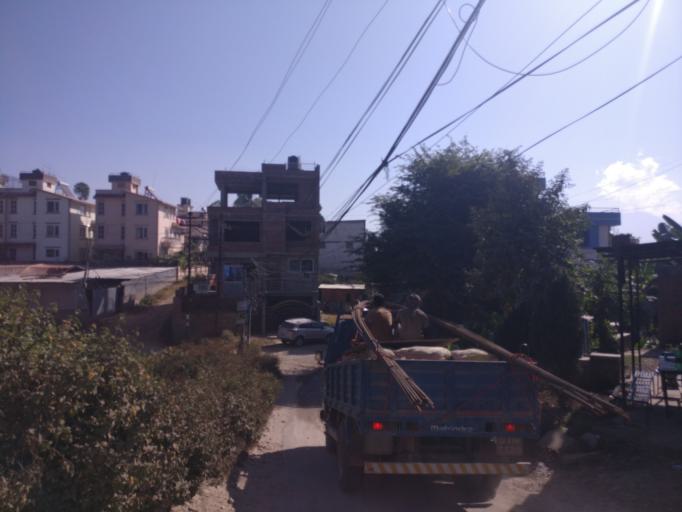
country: NP
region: Central Region
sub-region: Bagmati Zone
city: Patan
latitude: 27.6492
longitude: 85.3064
